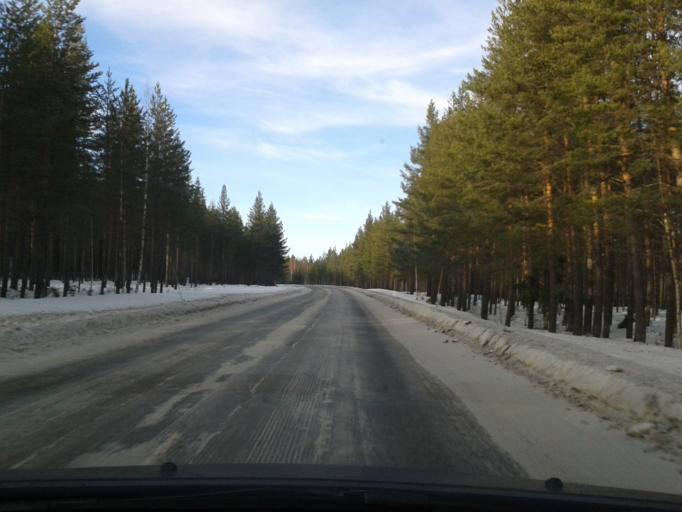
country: SE
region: Vaesternorrland
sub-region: OErnskoeldsviks Kommun
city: Bredbyn
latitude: 63.5346
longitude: 17.9662
